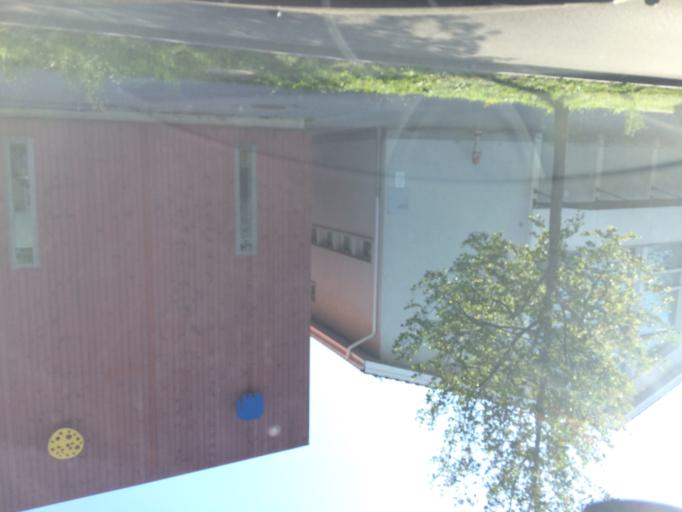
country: CH
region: Bern
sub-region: Thun District
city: Thun
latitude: 46.7398
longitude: 7.6213
